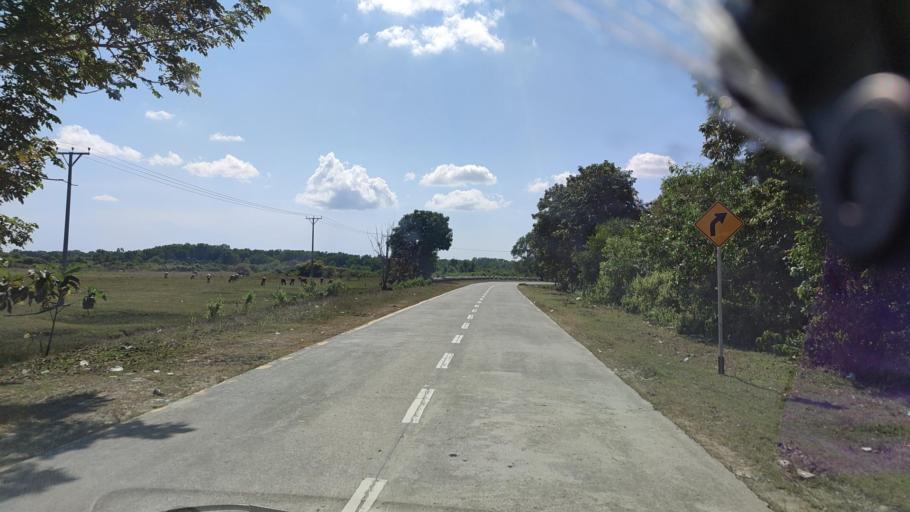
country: MM
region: Rakhine
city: Sittwe
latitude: 20.2829
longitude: 92.8696
